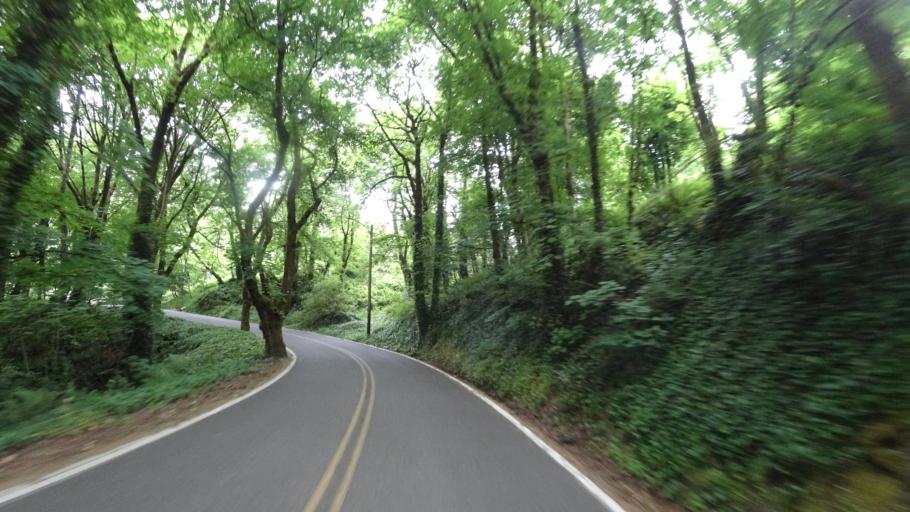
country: US
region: Oregon
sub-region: Multnomah County
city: Portland
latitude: 45.4920
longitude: -122.7006
